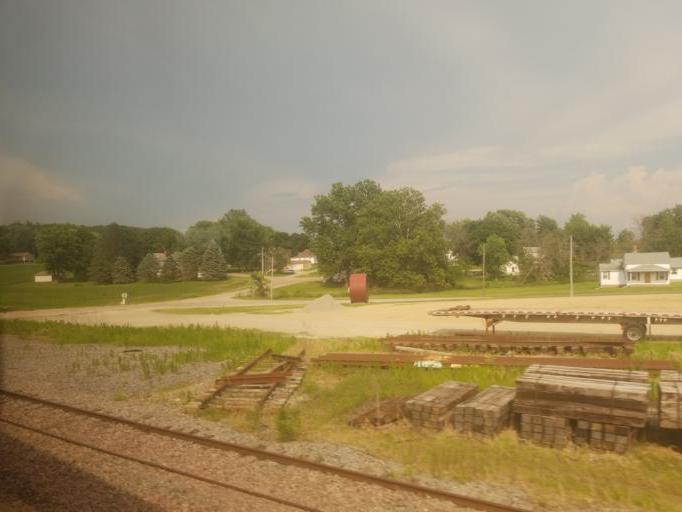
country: US
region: Illinois
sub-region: Bureau County
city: Princeton
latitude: 41.3264
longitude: -89.6780
